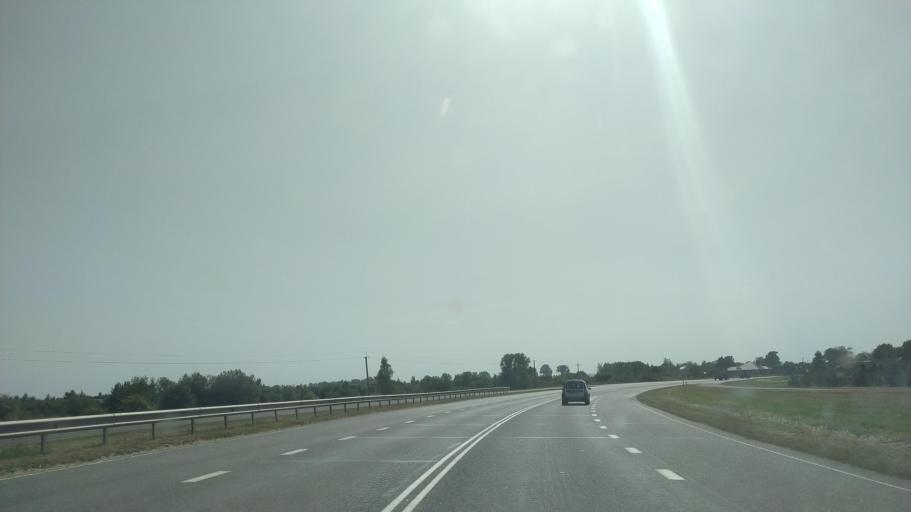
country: BY
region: Brest
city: Byaroza
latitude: 52.4873
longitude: 24.9692
